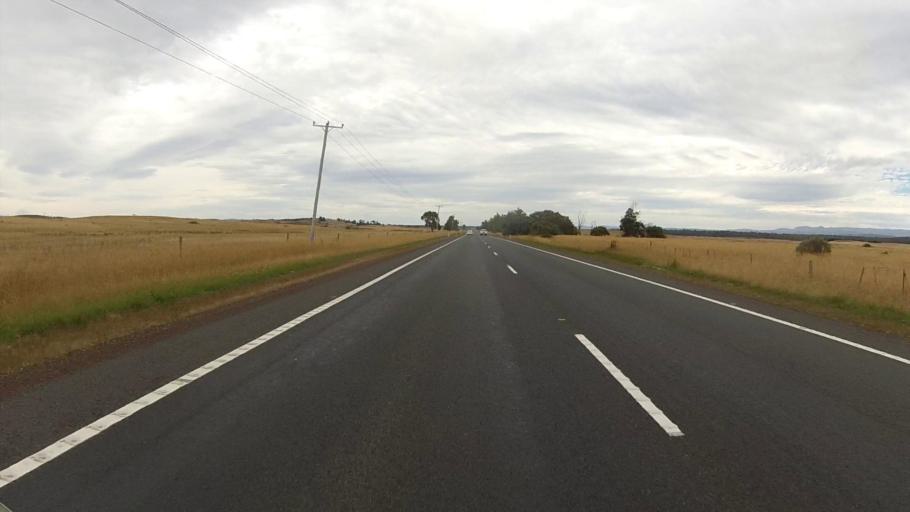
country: AU
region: Tasmania
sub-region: Northern Midlands
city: Evandale
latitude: -41.8939
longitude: 147.4723
